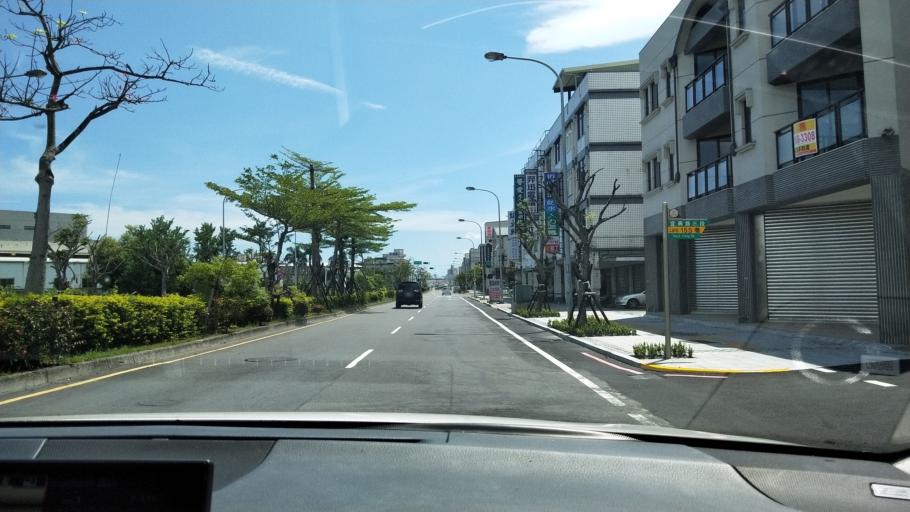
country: TW
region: Taiwan
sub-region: Yilan
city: Yilan
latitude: 24.7704
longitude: 121.7588
